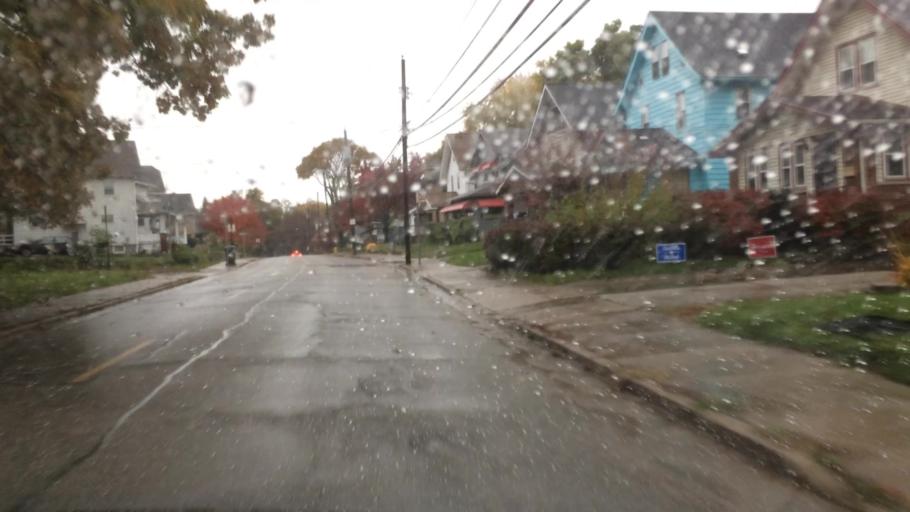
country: US
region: Ohio
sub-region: Summit County
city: Akron
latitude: 41.0983
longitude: -81.5077
